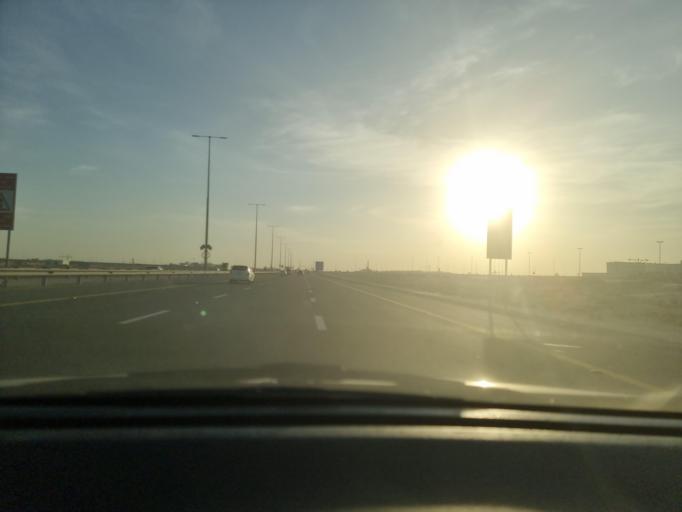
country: AE
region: Abu Dhabi
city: Abu Dhabi
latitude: 24.3427
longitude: 54.7027
